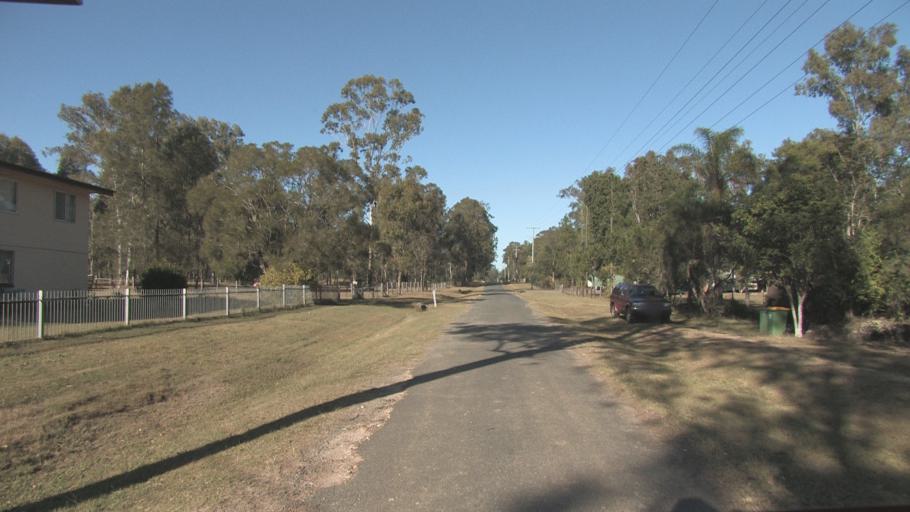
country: AU
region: Queensland
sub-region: Logan
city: Park Ridge South
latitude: -27.7503
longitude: 153.0346
